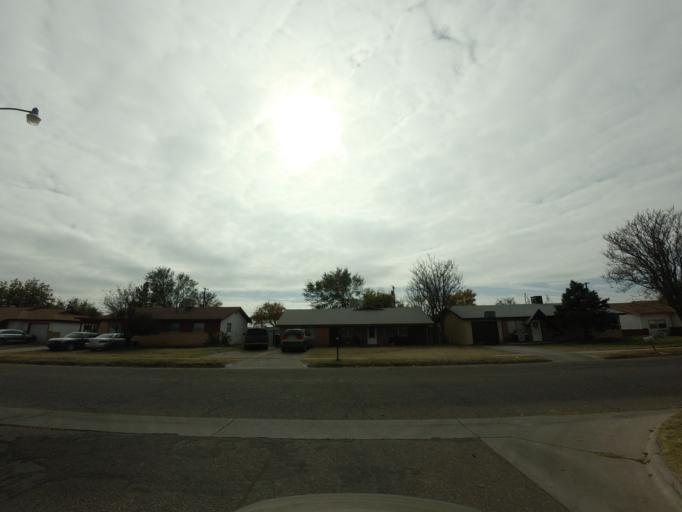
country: US
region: New Mexico
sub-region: Curry County
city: Clovis
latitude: 34.4279
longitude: -103.2216
